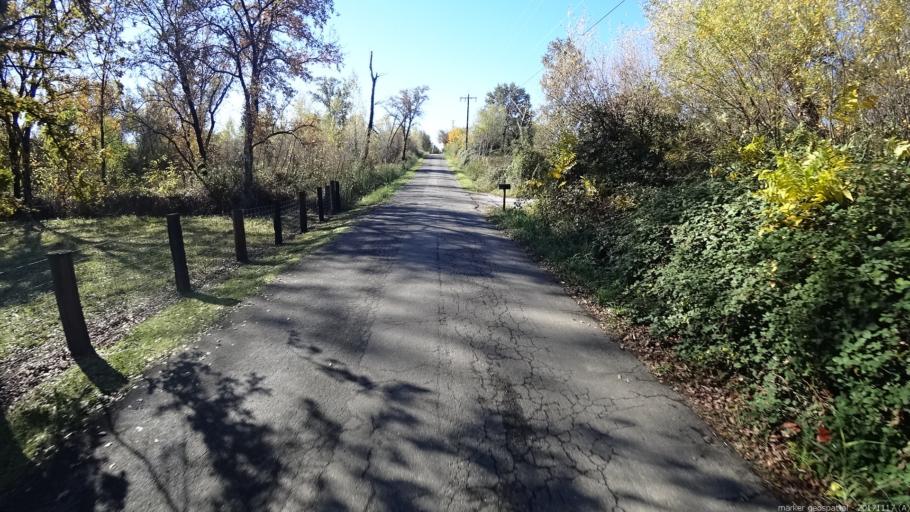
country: US
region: California
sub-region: Shasta County
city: Cottonwood
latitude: 40.4280
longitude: -122.2227
